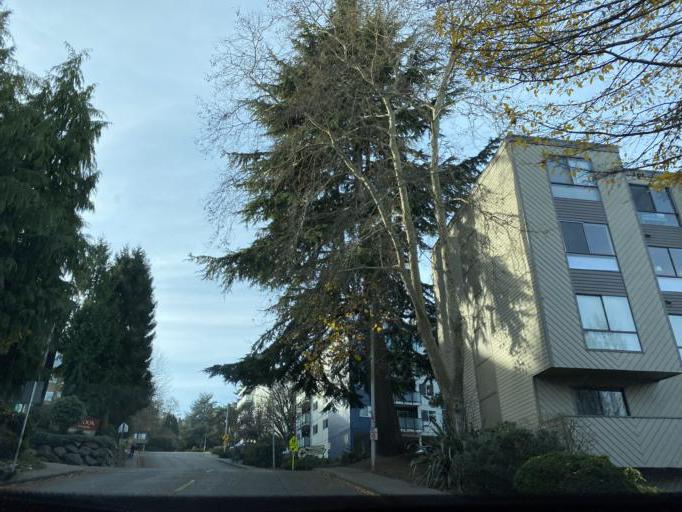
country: US
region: Washington
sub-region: King County
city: Seattle
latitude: 47.6534
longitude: -122.3896
